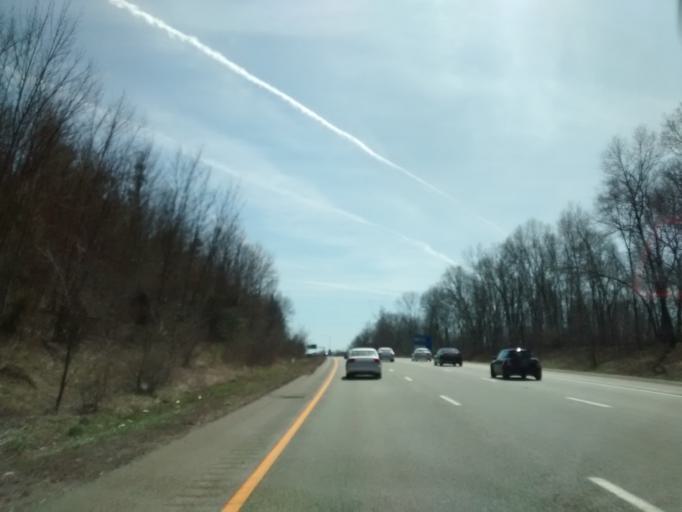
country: US
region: Massachusetts
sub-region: Worcester County
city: Southborough
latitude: 42.2954
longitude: -71.5678
